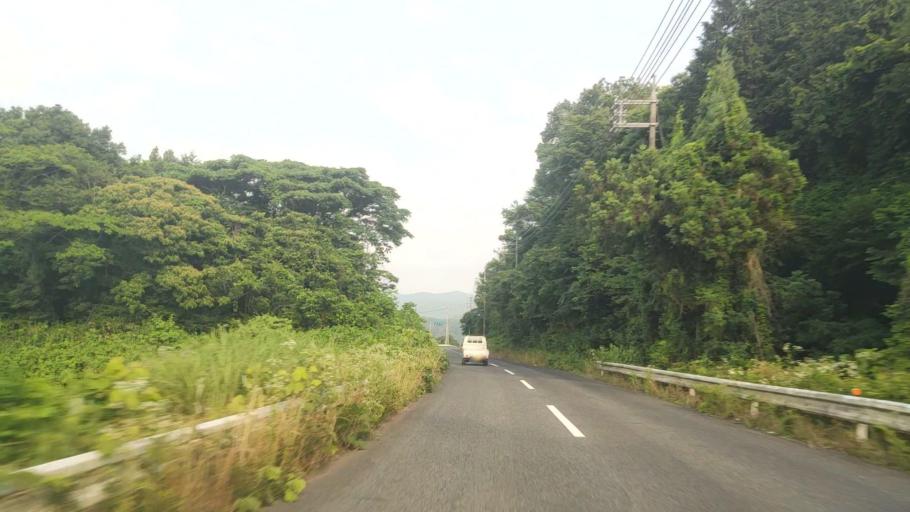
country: JP
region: Tottori
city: Kurayoshi
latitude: 35.3965
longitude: 133.7741
